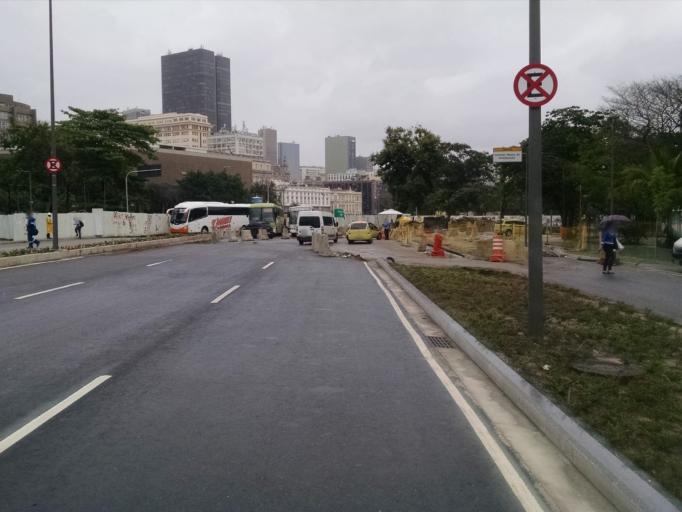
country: BR
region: Rio de Janeiro
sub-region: Rio De Janeiro
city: Rio de Janeiro
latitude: -22.9052
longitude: -43.1693
